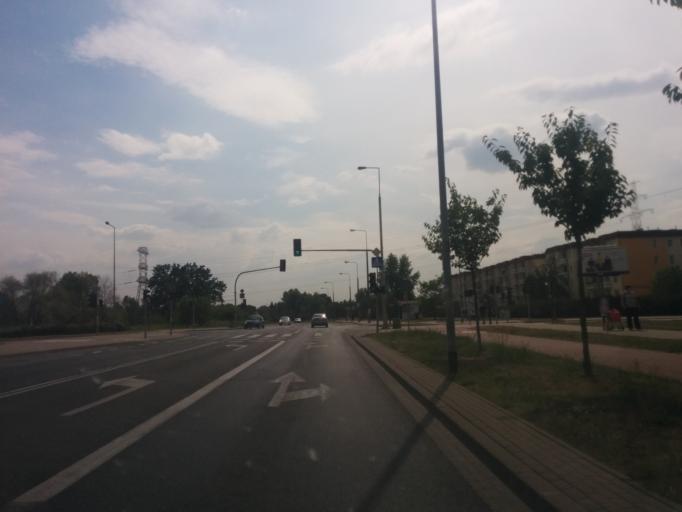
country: PL
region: Masovian Voivodeship
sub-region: Warszawa
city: Bialoleka
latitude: 52.3280
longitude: 20.9407
